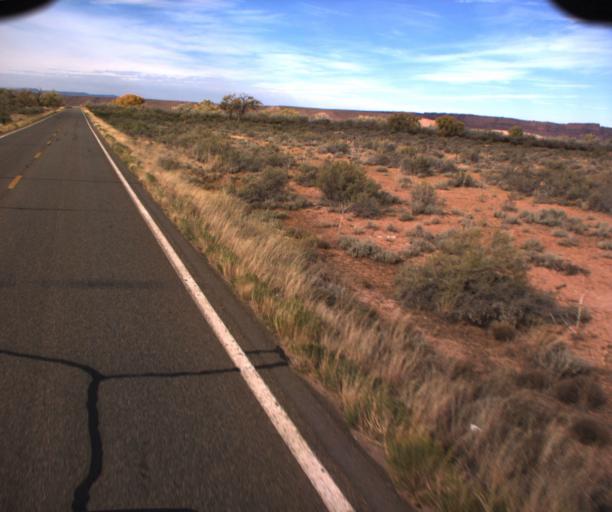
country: US
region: Arizona
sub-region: Apache County
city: Many Farms
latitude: 36.4654
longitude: -109.5855
